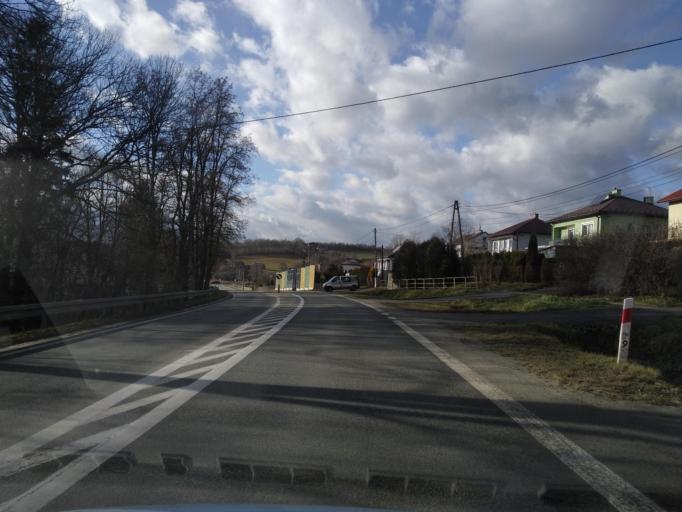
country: PL
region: Subcarpathian Voivodeship
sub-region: Powiat jasielski
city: Skolyszyn
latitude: 49.7575
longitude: 21.3027
